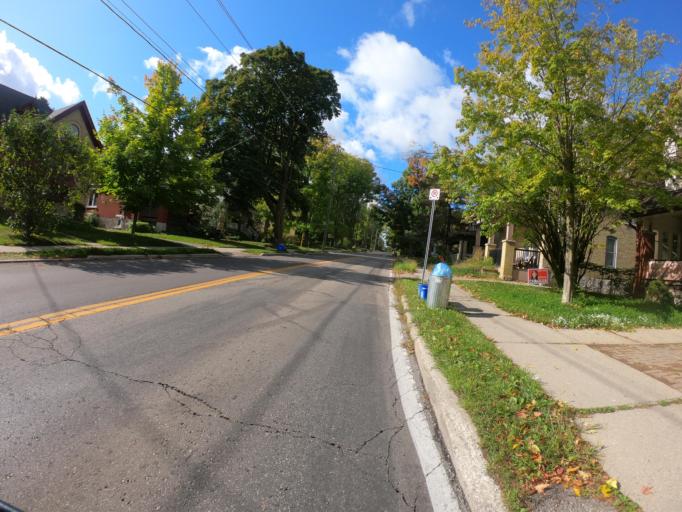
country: CA
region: Ontario
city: Waterloo
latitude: 43.4583
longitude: -80.5252
